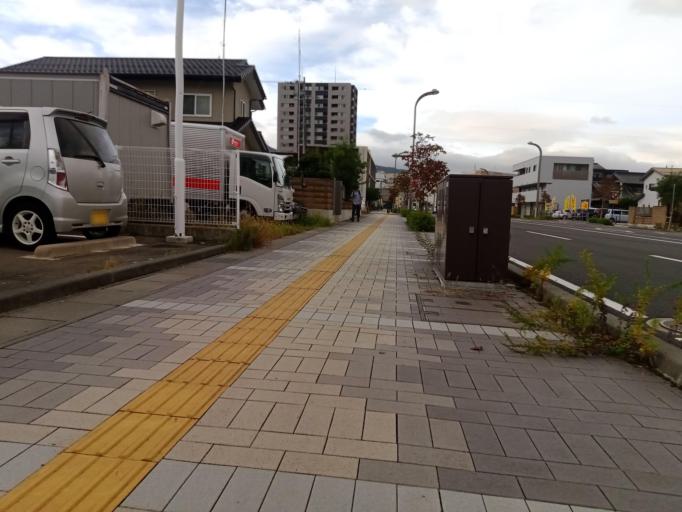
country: JP
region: Nagano
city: Nagano-shi
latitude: 36.6381
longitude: 138.1874
